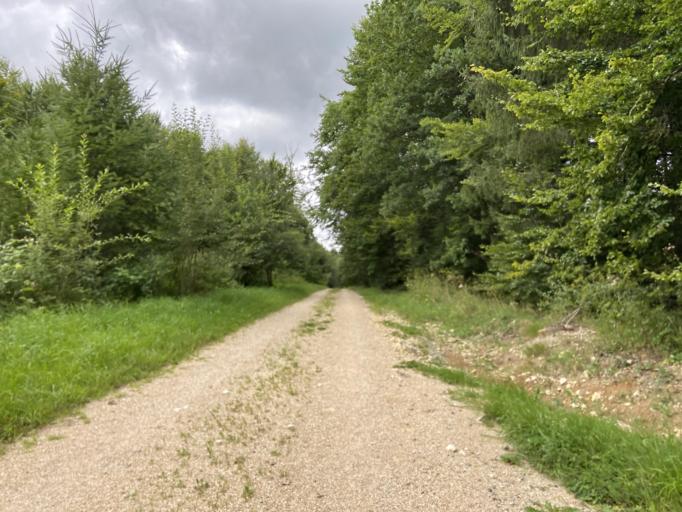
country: DE
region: Baden-Wuerttemberg
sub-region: Tuebingen Region
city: Sigmaringendorf
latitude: 48.0856
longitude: 9.2715
